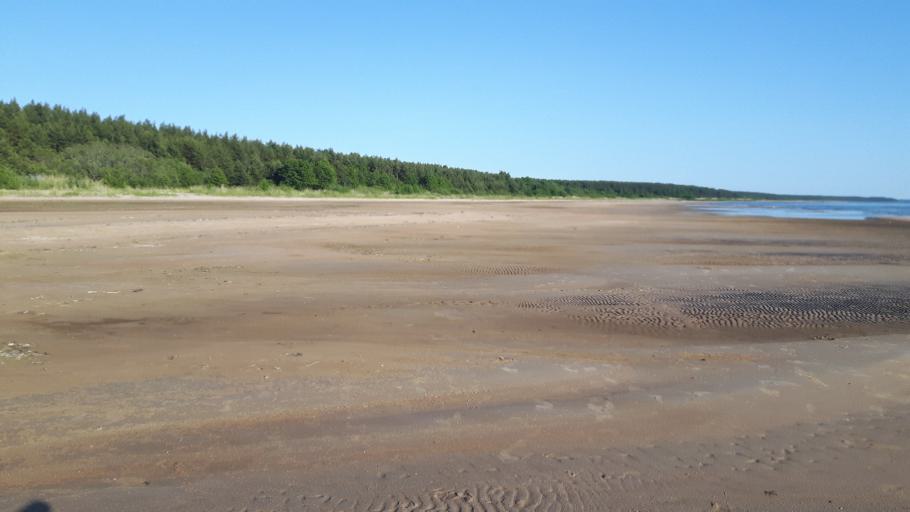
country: LV
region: Salacgrivas
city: Salacgriva
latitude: 57.6925
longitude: 24.3521
